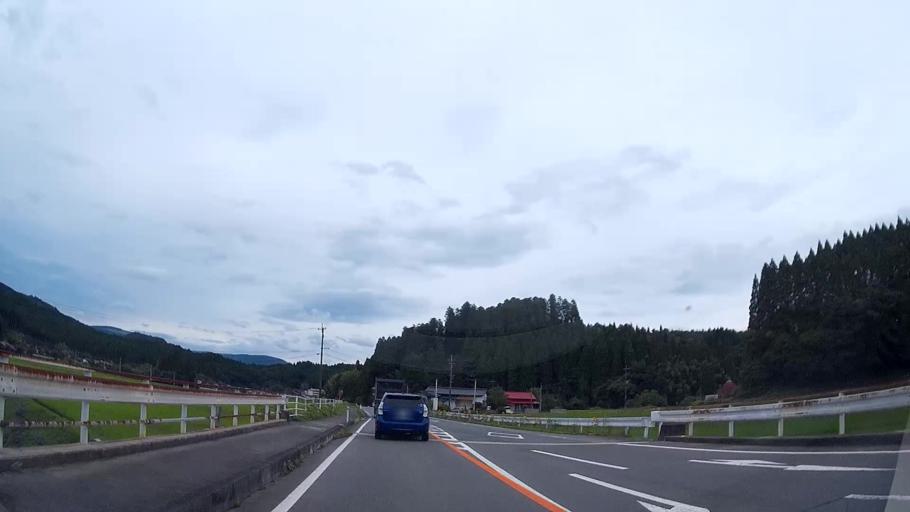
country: JP
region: Kumamoto
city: Aso
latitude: 33.1239
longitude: 131.0297
